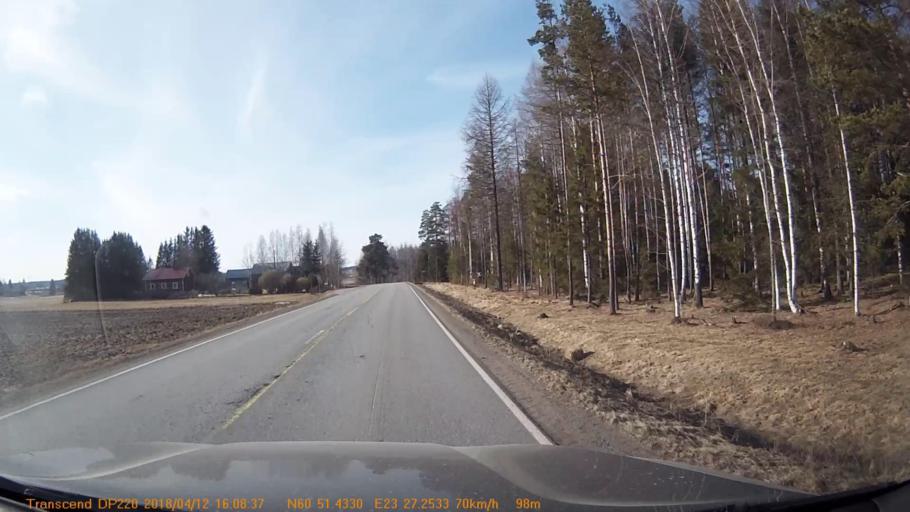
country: FI
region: Haeme
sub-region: Forssa
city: Jokioinen
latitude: 60.8571
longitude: 23.4544
